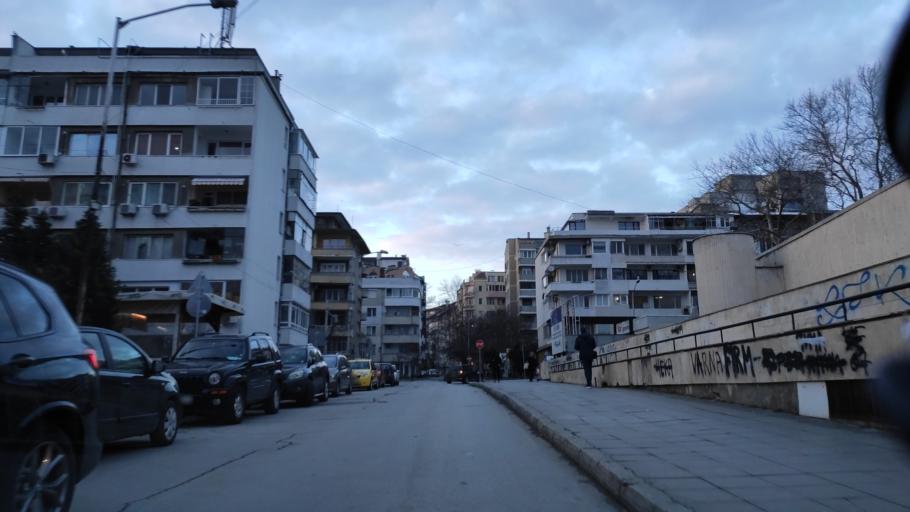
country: BG
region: Varna
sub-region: Obshtina Varna
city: Varna
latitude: 43.2107
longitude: 27.9297
